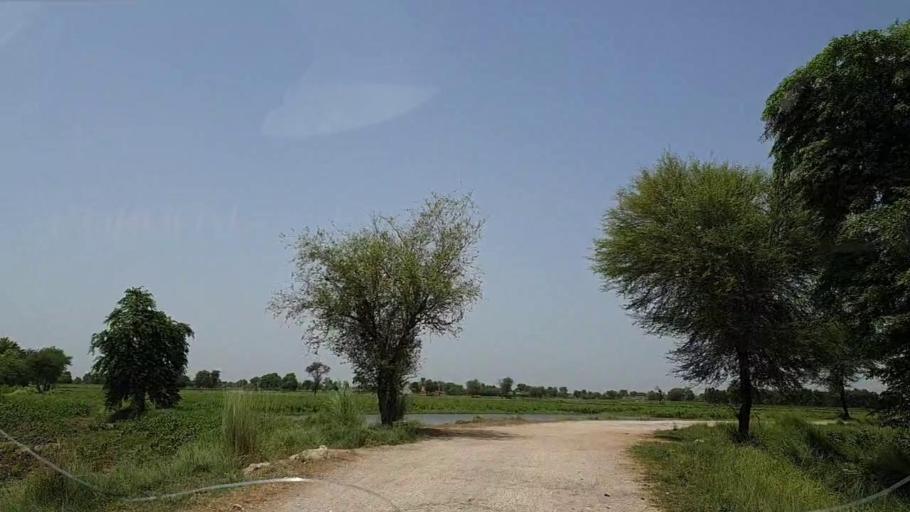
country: PK
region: Sindh
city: Tharu Shah
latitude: 26.9300
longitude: 68.0510
